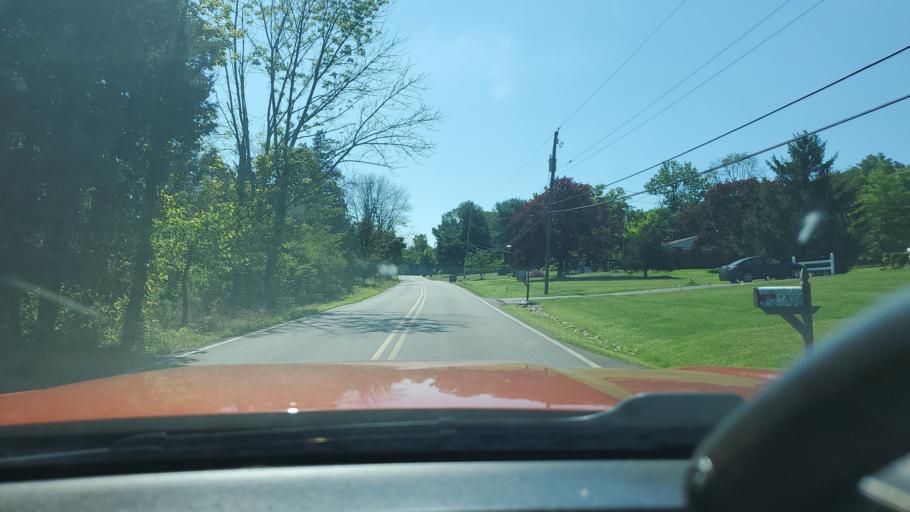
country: US
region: Pennsylvania
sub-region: Montgomery County
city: Red Hill
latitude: 40.3512
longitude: -75.5231
